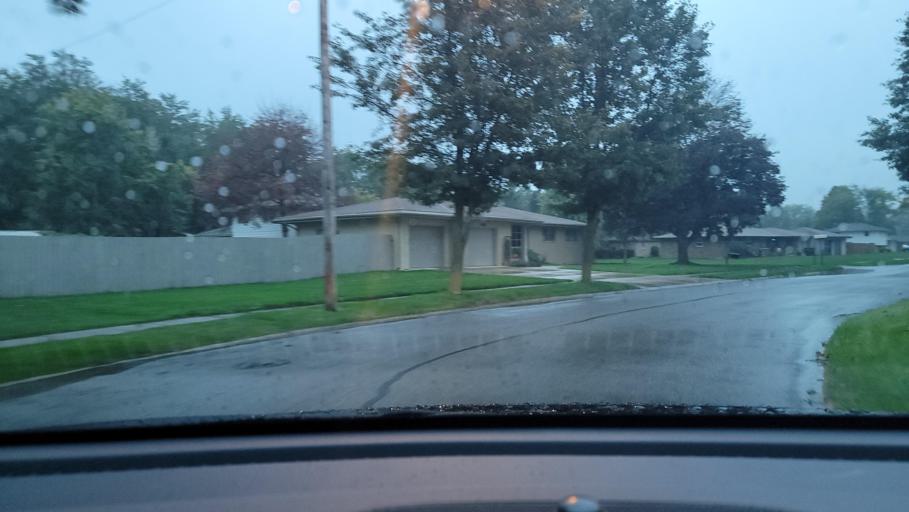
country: US
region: Indiana
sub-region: Porter County
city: Portage
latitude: 41.5683
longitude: -87.1922
